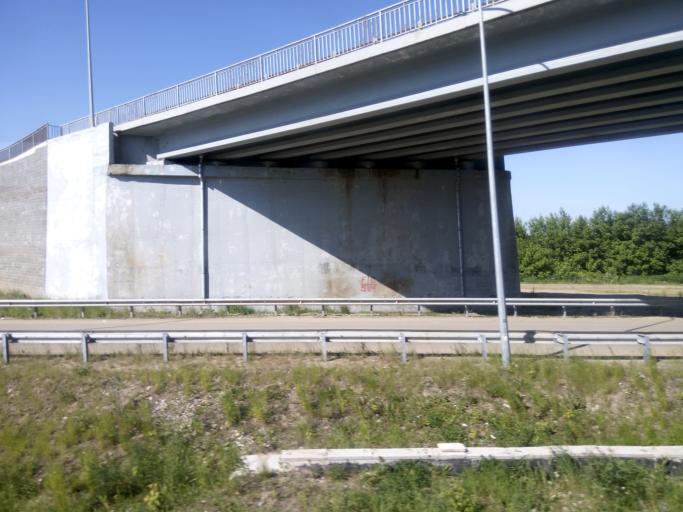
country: RU
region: Tatarstan
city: Stolbishchi
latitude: 55.6673
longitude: 49.2172
